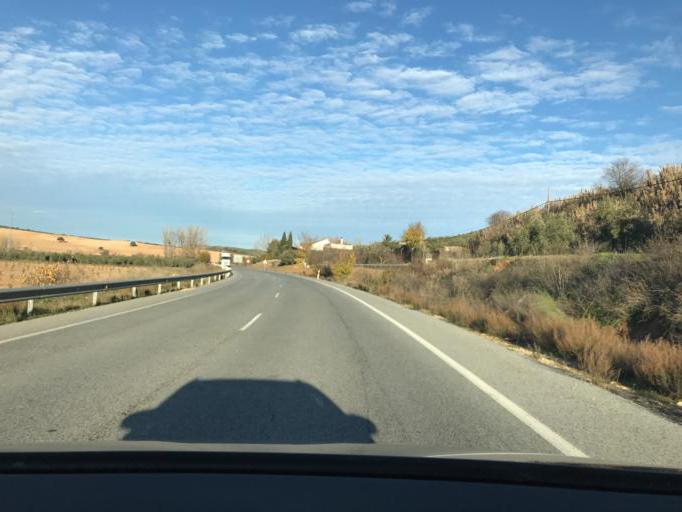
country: ES
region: Andalusia
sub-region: Provincia de Granada
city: Iznalloz
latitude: 37.4063
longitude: -3.5018
